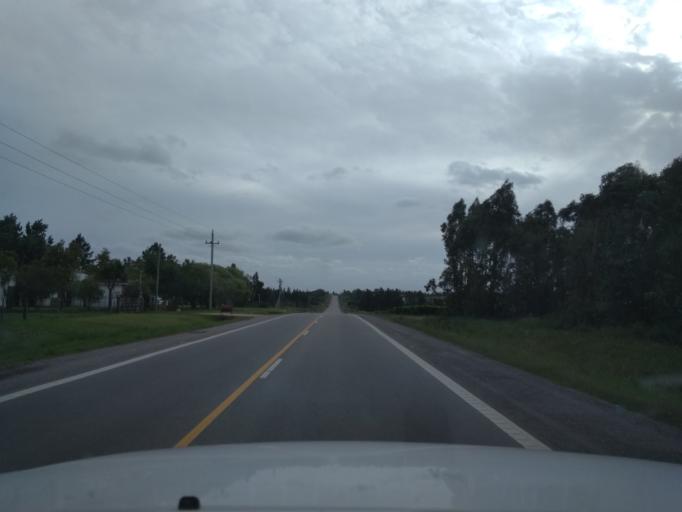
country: UY
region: Canelones
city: Joaquin Suarez
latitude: -34.6926
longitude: -56.0306
